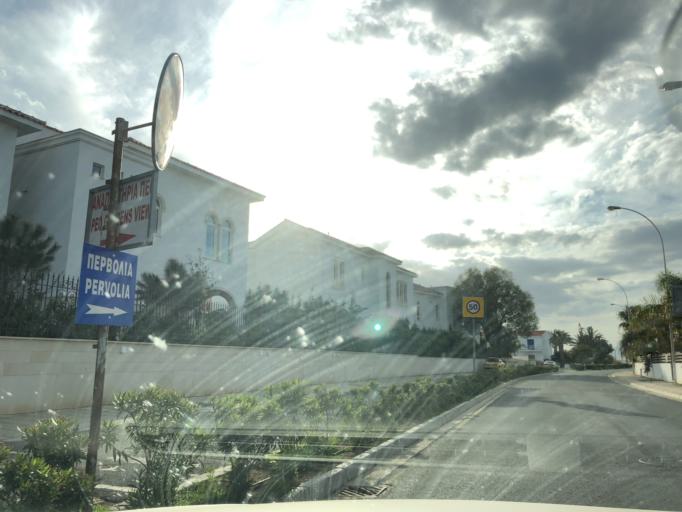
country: CY
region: Larnaka
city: Perivolia
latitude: 34.8173
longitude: 33.6002
